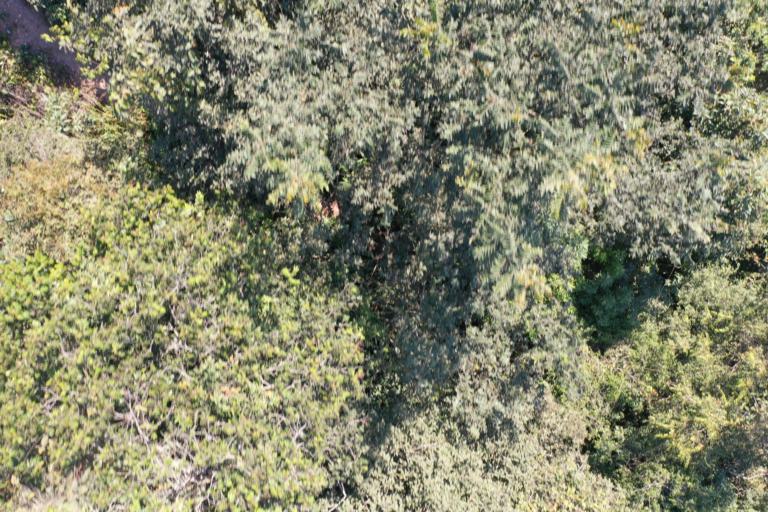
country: BO
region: La Paz
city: Mapiri
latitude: -15.3052
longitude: -68.2143
